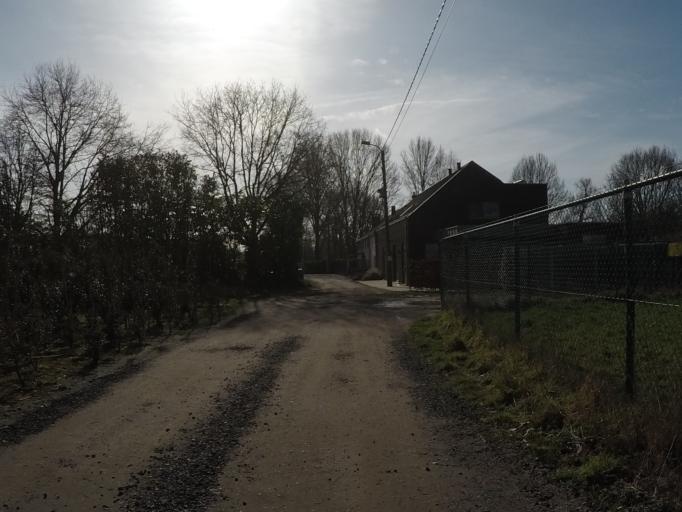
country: BE
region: Flanders
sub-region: Provincie Antwerpen
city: Ranst
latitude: 51.2035
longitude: 4.5473
